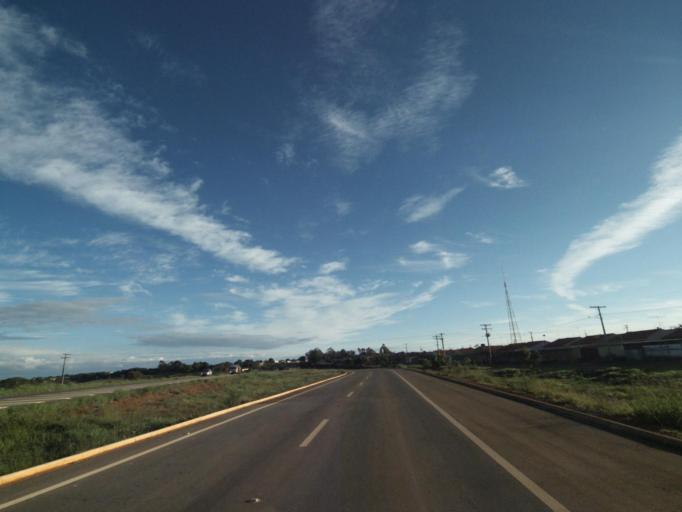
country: BR
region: Federal District
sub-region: Brasilia
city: Brasilia
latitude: -15.7475
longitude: -48.4112
